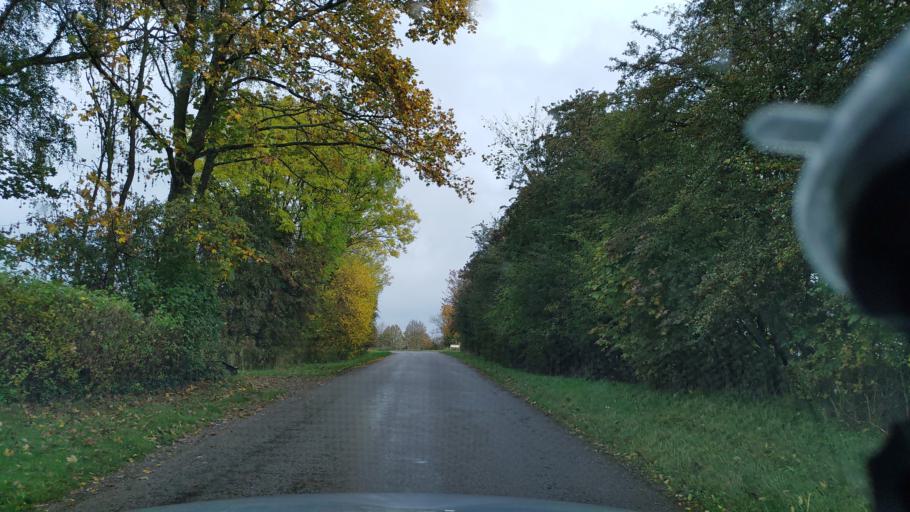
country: DK
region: Zealand
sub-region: Faxe Kommune
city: Ronnede
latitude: 55.2581
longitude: 11.9625
